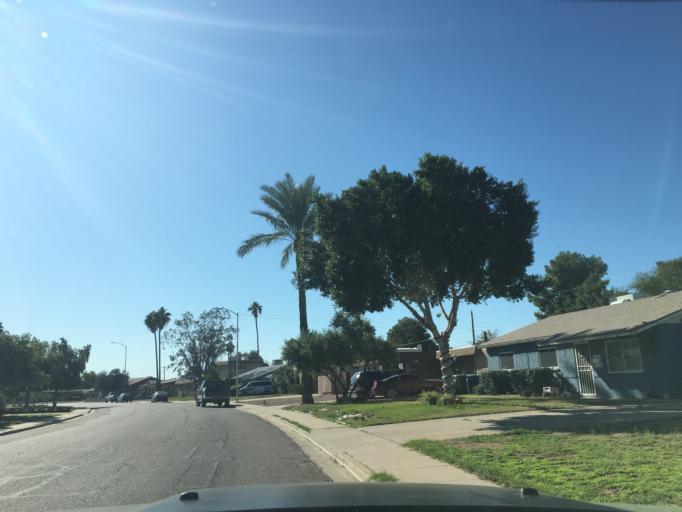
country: US
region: Arizona
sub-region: Maricopa County
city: Mesa
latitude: 33.4462
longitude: -111.8504
